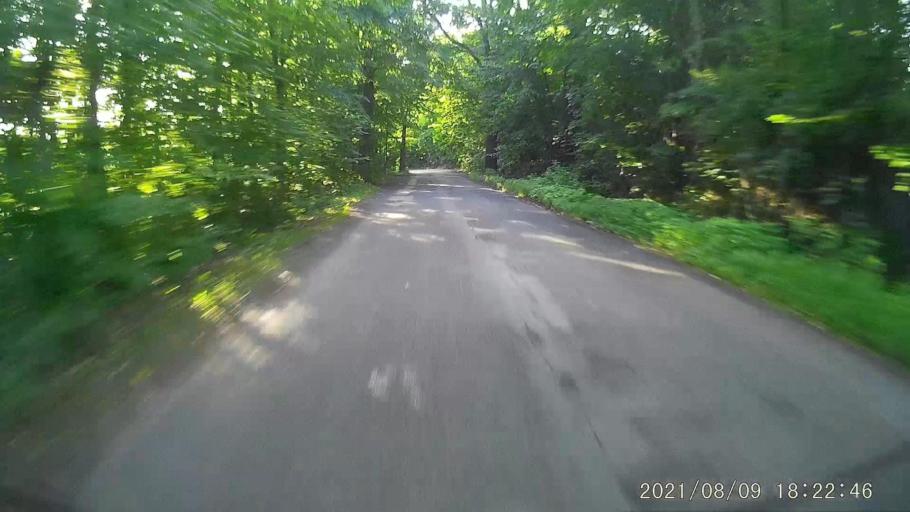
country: PL
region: Lower Silesian Voivodeship
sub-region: Powiat zabkowicki
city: Bardo
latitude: 50.5034
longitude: 16.7138
